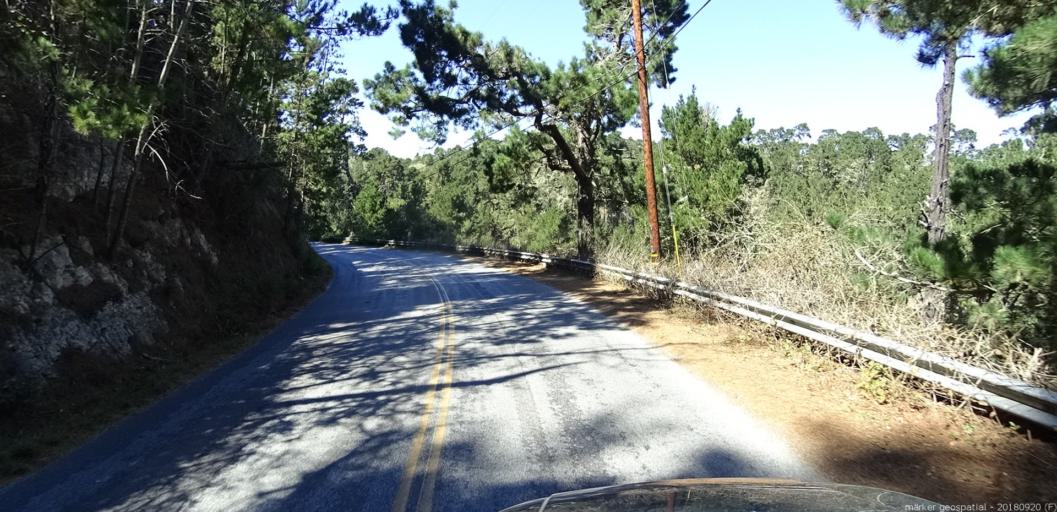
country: US
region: California
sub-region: Monterey County
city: Carmel-by-the-Sea
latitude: 36.5699
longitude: -121.9005
